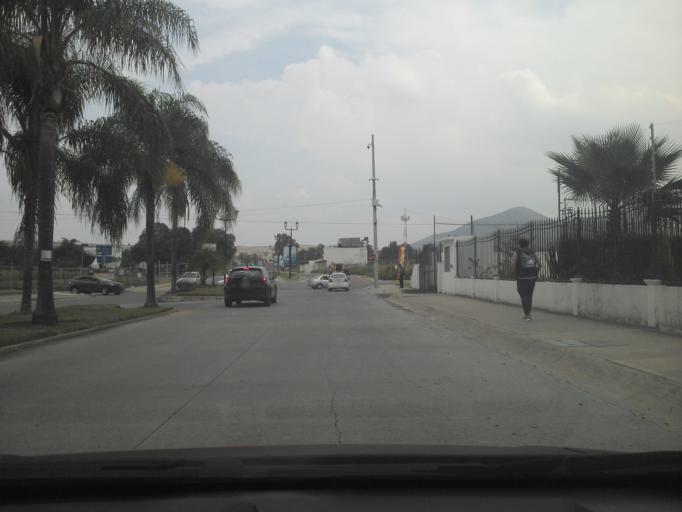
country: MX
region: Jalisco
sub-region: Tlajomulco de Zuniga
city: Lomas de San Agustin
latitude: 20.5303
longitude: -103.4697
